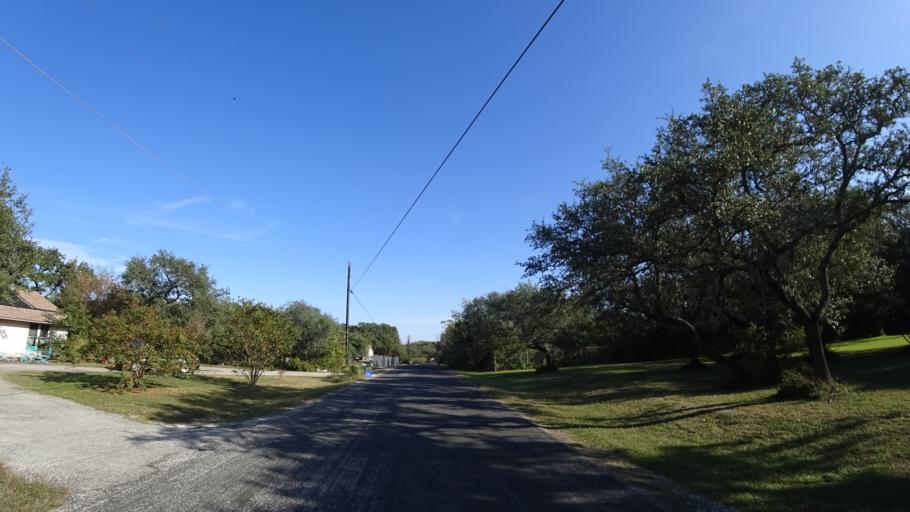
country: US
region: Texas
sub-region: Travis County
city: Barton Creek
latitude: 30.2393
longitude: -97.9103
